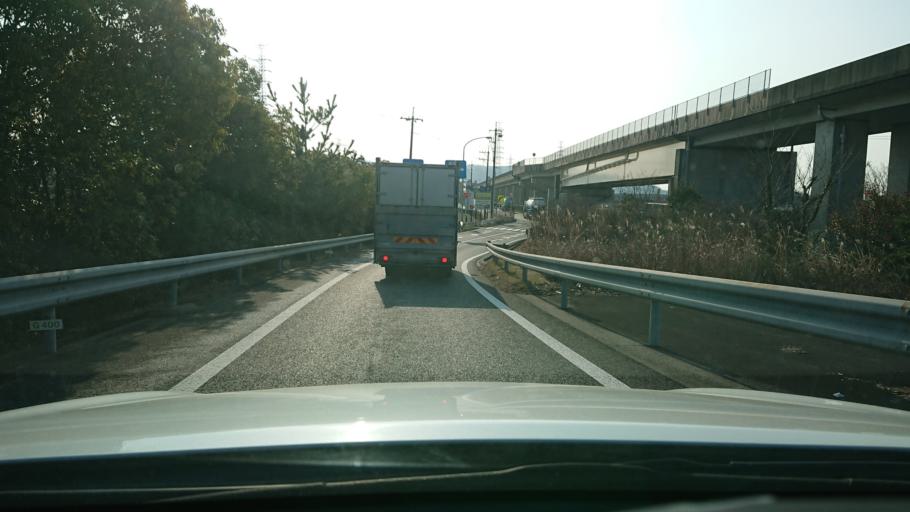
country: JP
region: Okayama
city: Kurashiki
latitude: 34.5790
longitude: 133.6869
